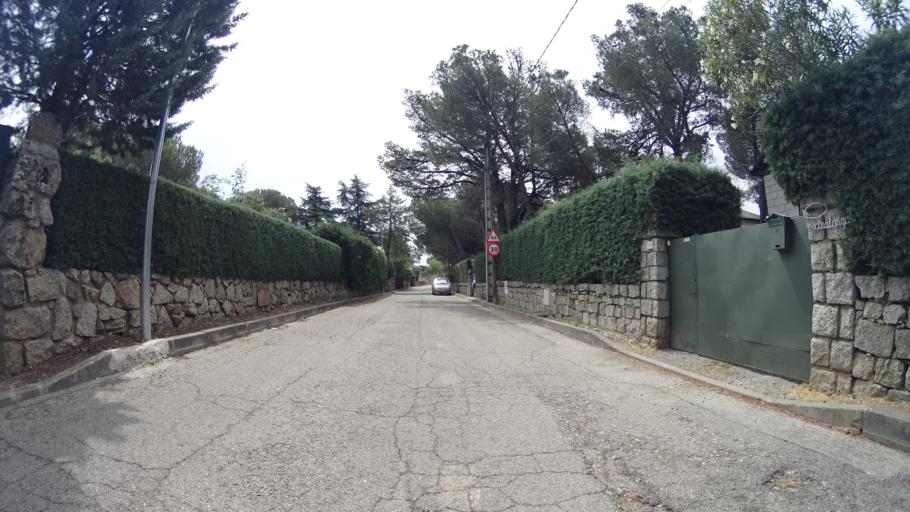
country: ES
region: Madrid
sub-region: Provincia de Madrid
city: Galapagar
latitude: 40.5711
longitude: -4.0016
